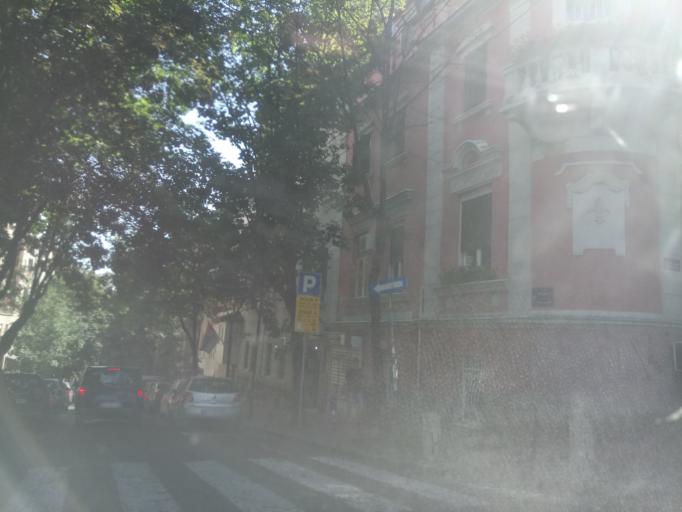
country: RS
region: Central Serbia
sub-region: Belgrade
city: Stari Grad
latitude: 44.8228
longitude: 20.4559
